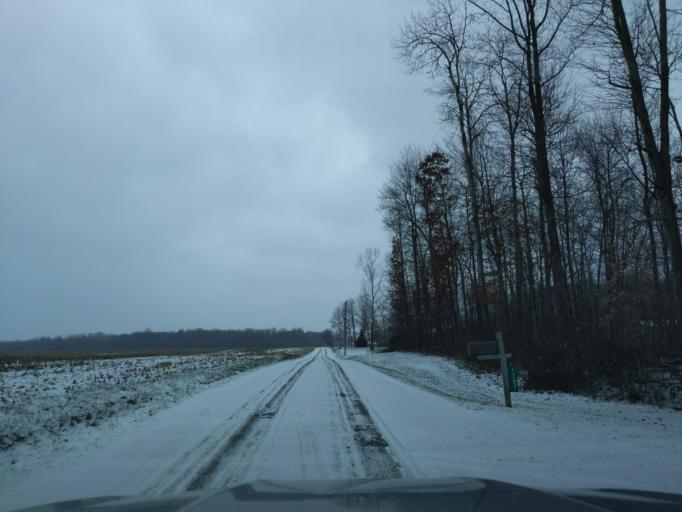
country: US
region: Indiana
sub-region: Decatur County
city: Westport
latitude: 39.2049
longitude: -85.5134
